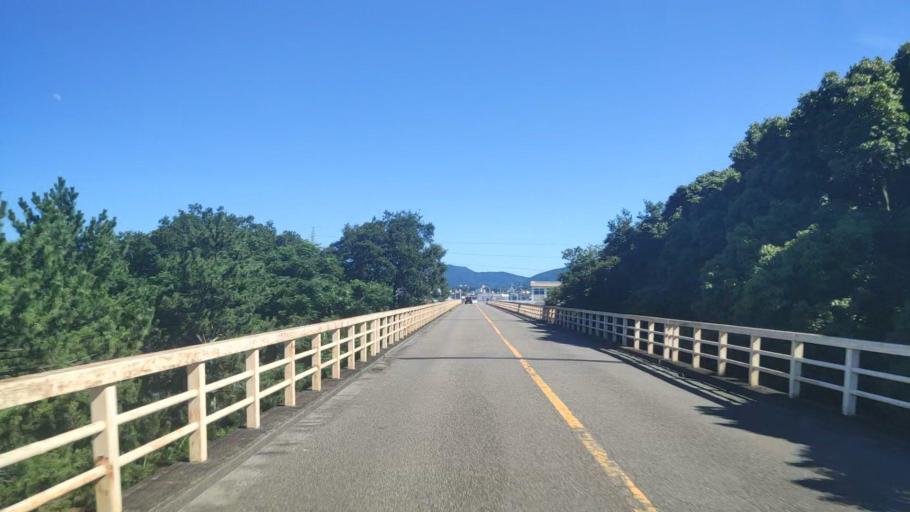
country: JP
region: Mie
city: Ise
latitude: 34.5093
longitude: 136.6937
